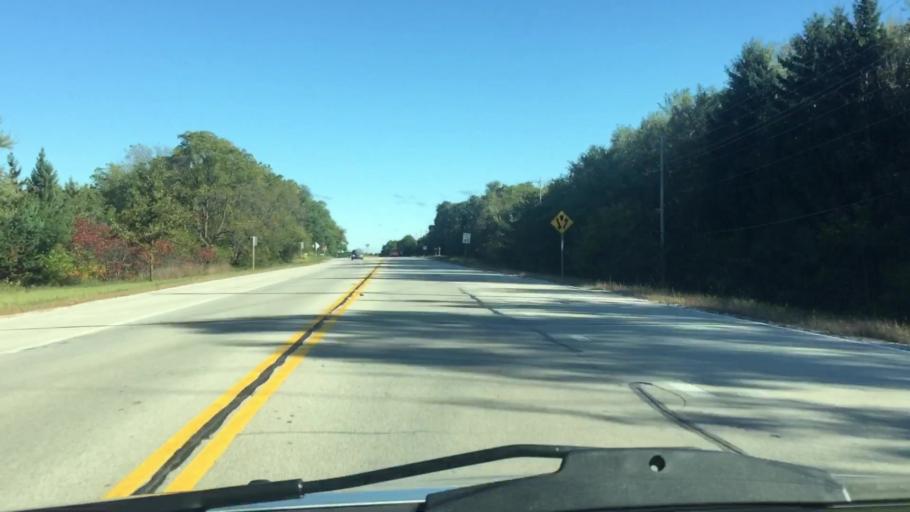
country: US
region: Wisconsin
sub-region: Waukesha County
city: Wales
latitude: 43.0404
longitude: -88.3739
